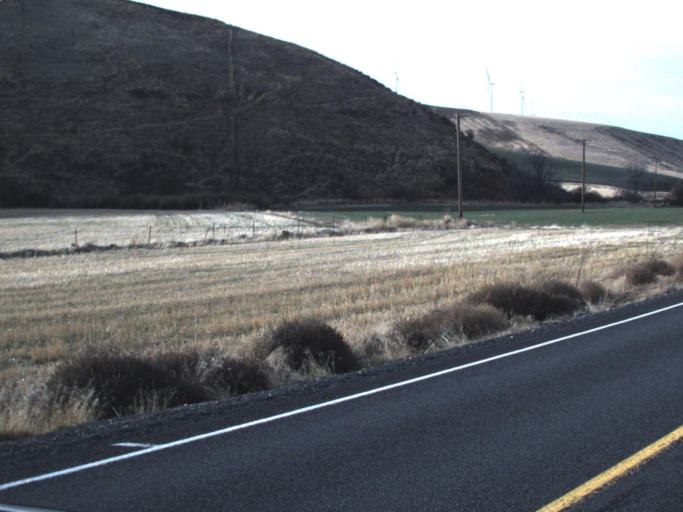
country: US
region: Washington
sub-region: Garfield County
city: Pomeroy
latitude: 46.5039
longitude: -117.7775
